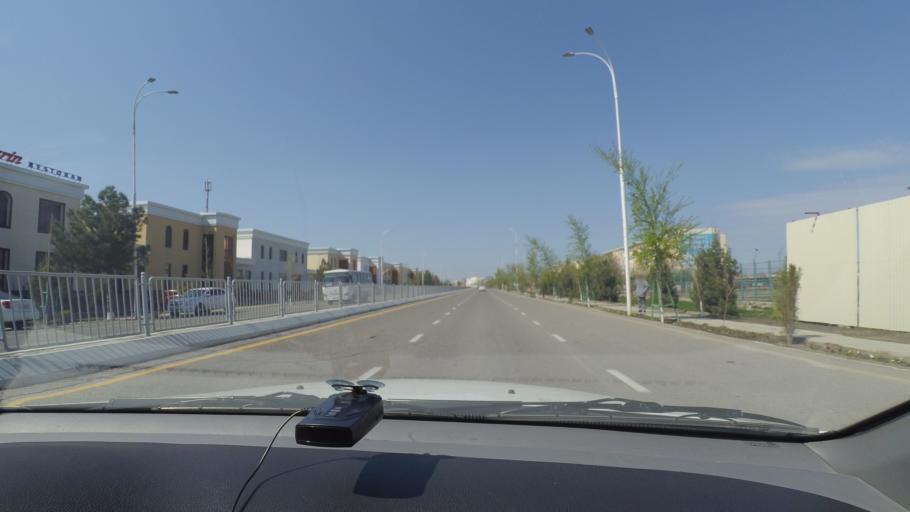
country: UZ
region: Bukhara
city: Bukhara
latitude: 39.7672
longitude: 64.4685
